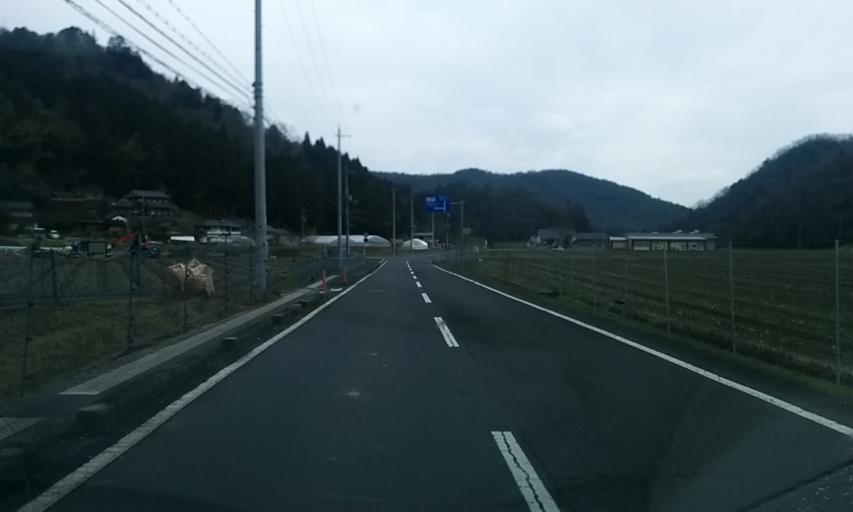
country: JP
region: Hyogo
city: Sasayama
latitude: 35.1307
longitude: 135.4120
